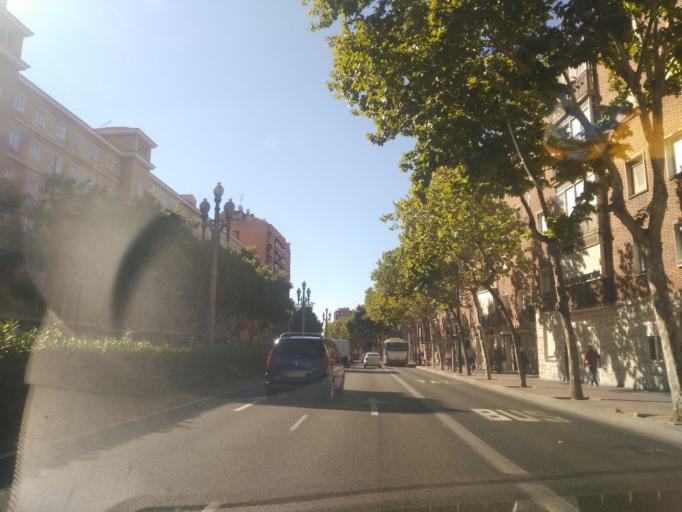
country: ES
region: Castille and Leon
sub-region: Provincia de Valladolid
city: Valladolid
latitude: 41.6365
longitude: -4.7393
